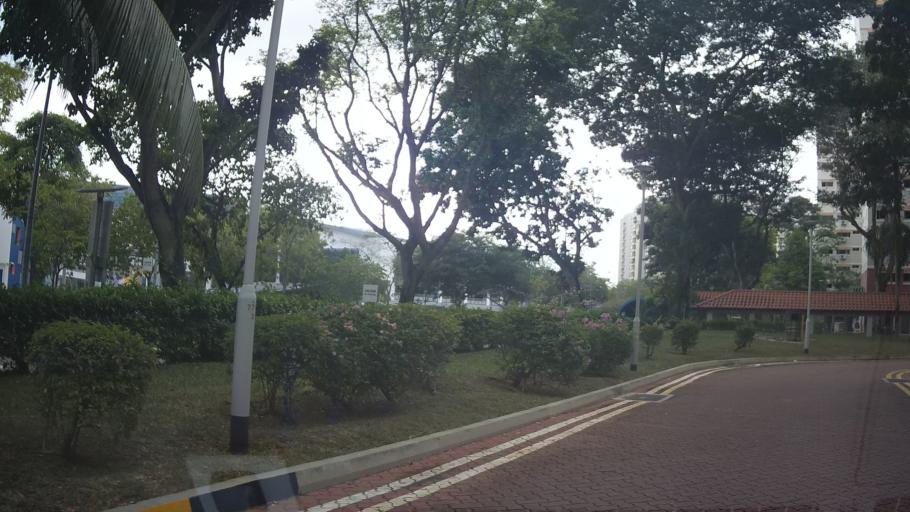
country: MY
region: Johor
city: Kampung Pasir Gudang Baru
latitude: 1.3760
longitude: 103.9363
